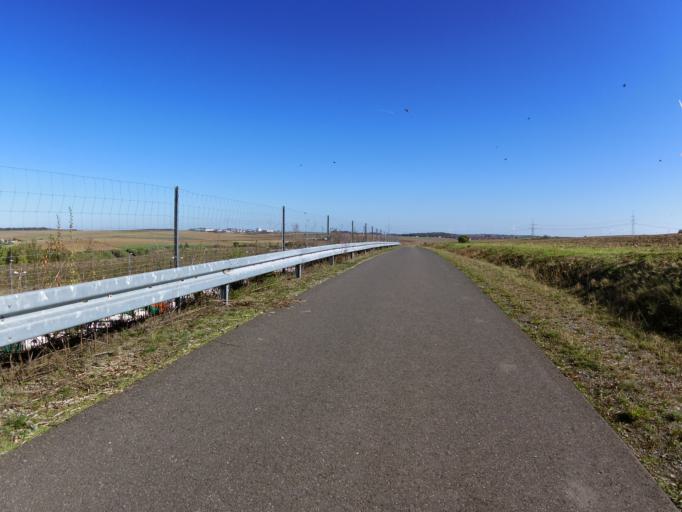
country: DE
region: Bavaria
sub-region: Regierungsbezirk Unterfranken
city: Theilheim
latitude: 49.7484
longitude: 10.0384
